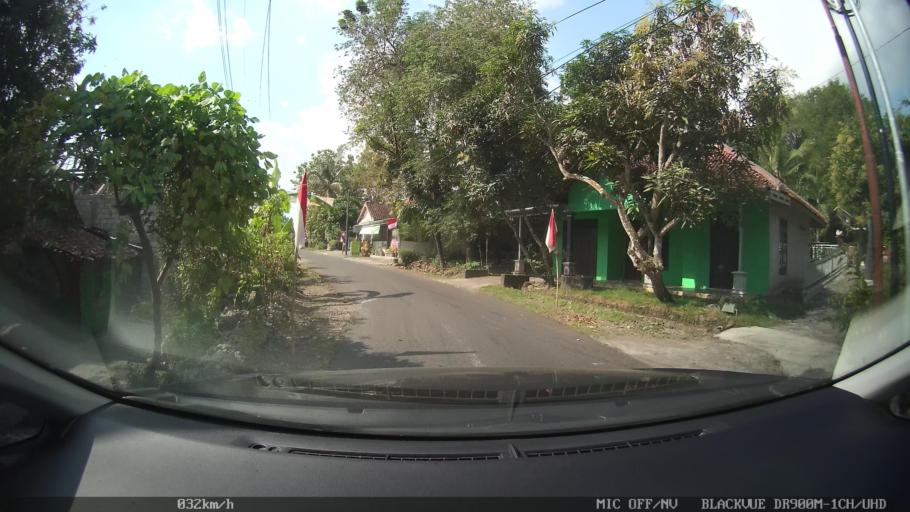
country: ID
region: Daerah Istimewa Yogyakarta
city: Kasihan
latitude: -7.8435
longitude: 110.3037
